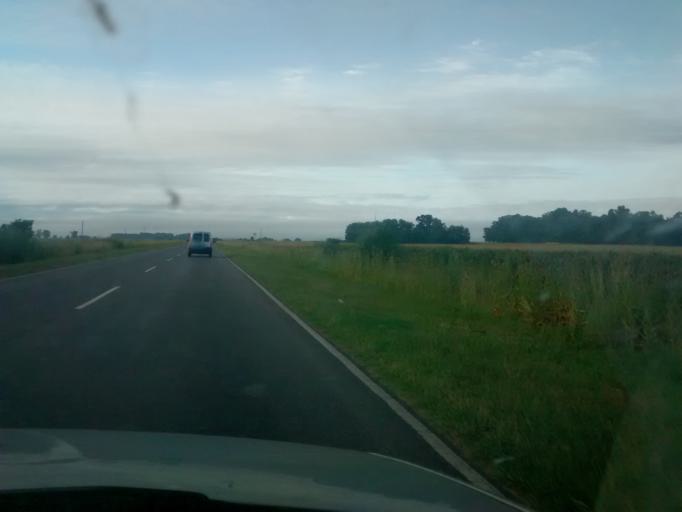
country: AR
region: Buenos Aires
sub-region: Partido de Brandsen
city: Brandsen
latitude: -35.3156
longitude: -58.2397
